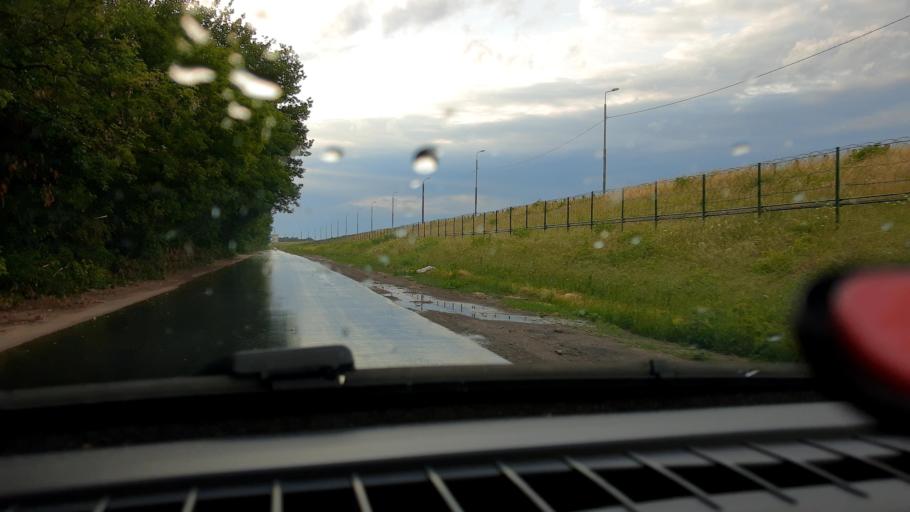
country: RU
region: Nizjnij Novgorod
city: Gorodets
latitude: 56.6655
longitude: 43.4328
